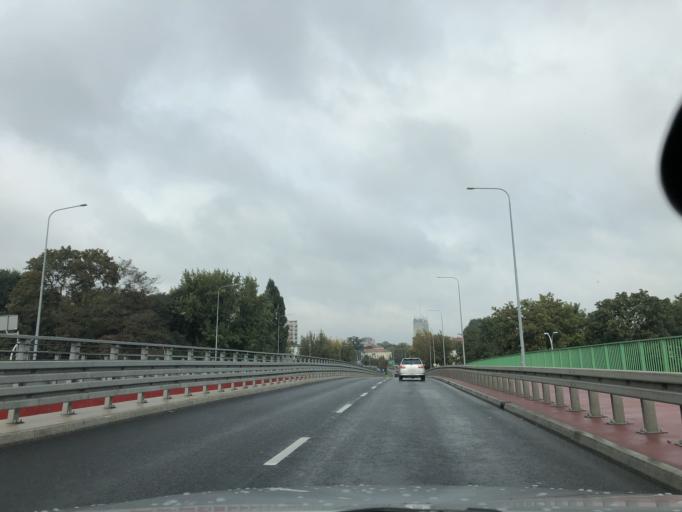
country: PL
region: Greater Poland Voivodeship
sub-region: Powiat pilski
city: Pila
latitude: 53.1432
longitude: 16.7401
